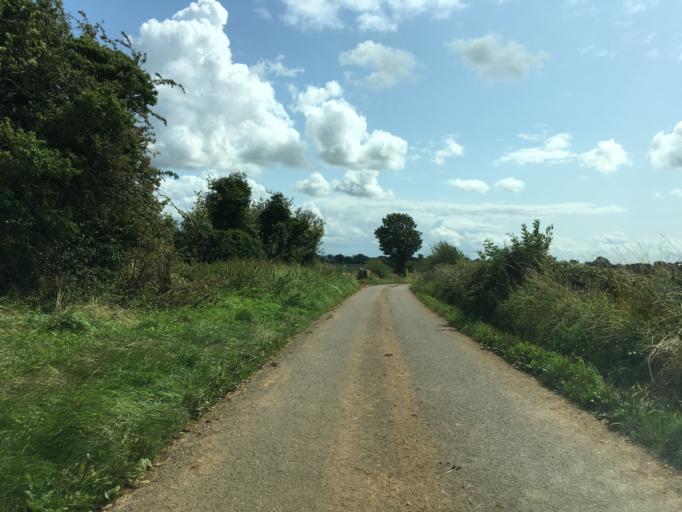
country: GB
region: England
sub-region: Wiltshire
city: Luckington
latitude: 51.6133
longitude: -2.2542
